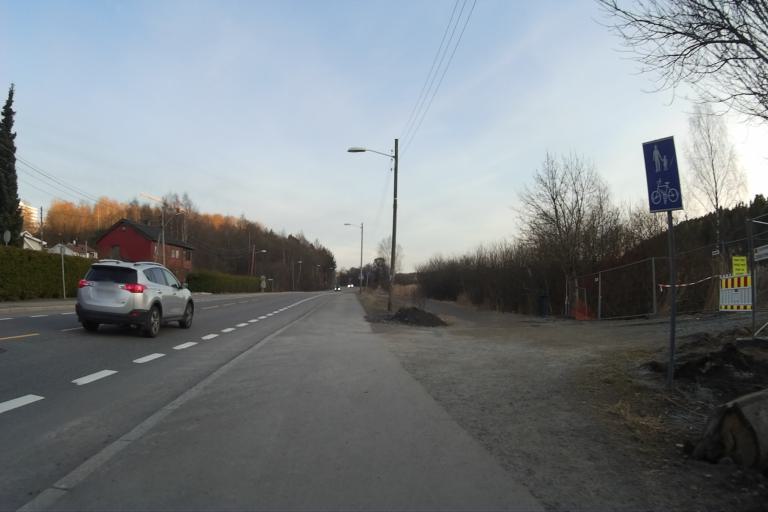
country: NO
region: Oslo
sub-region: Oslo
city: Oslo
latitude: 59.8971
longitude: 10.8328
